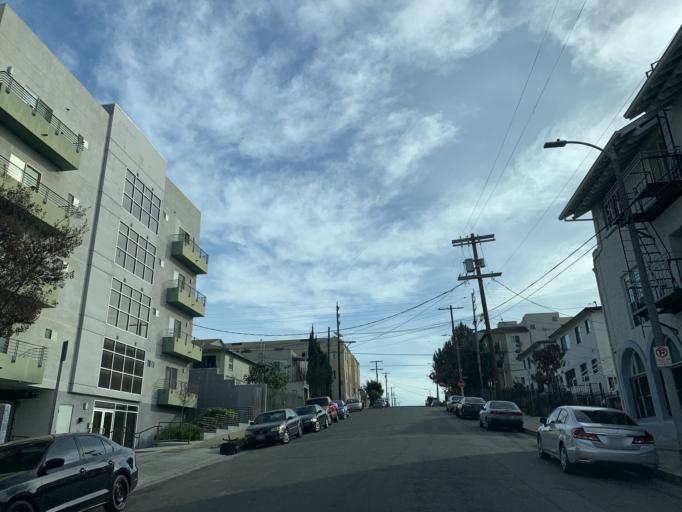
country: US
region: California
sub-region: Los Angeles County
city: Silver Lake
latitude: 34.0515
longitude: -118.3032
